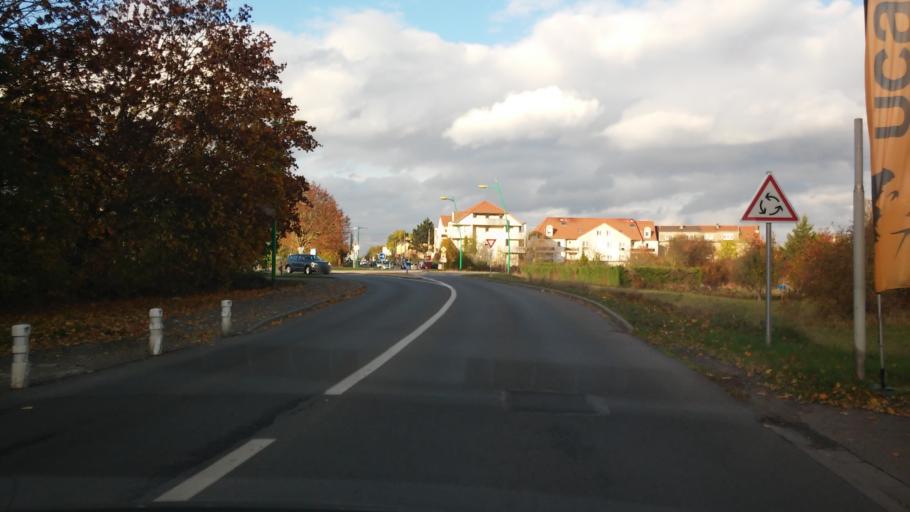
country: FR
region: Lorraine
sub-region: Departement de la Moselle
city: Talange
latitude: 49.2255
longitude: 6.1667
